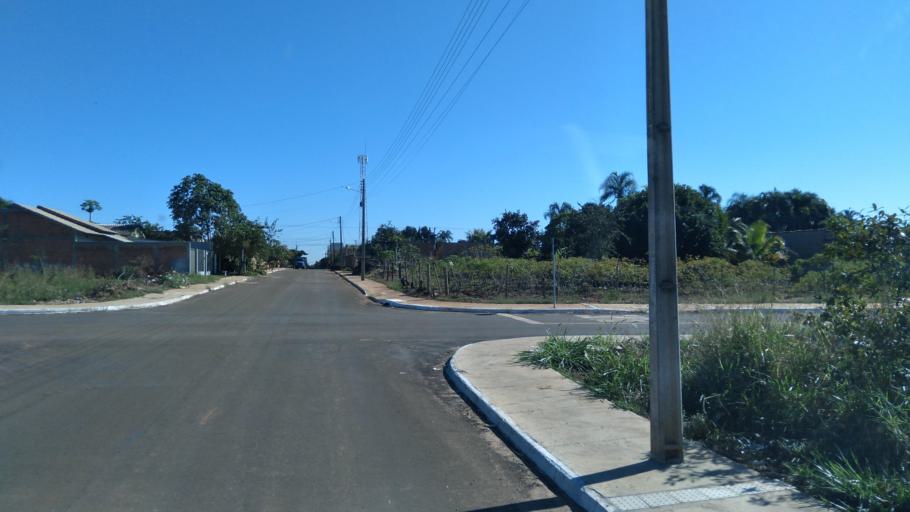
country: BR
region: Goias
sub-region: Mineiros
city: Mineiros
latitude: -17.5901
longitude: -52.5548
